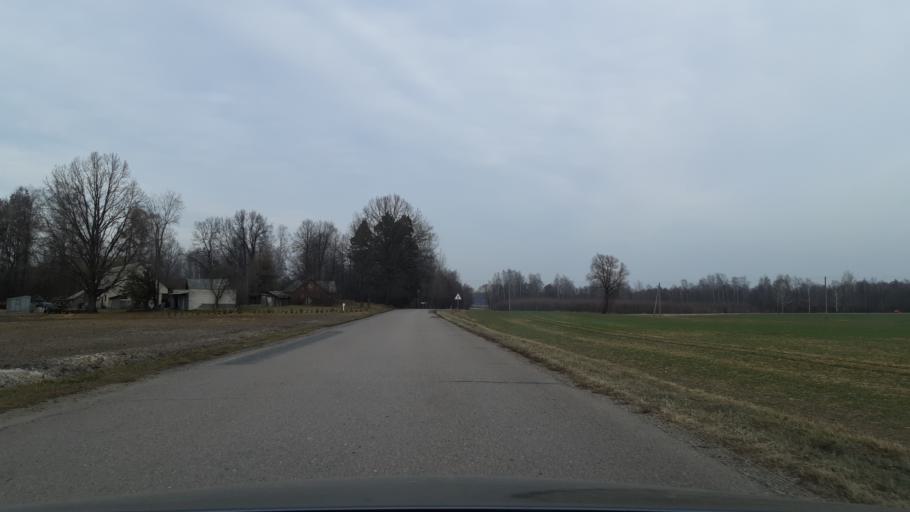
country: LT
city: Kazlu Ruda
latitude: 54.7312
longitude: 23.3392
